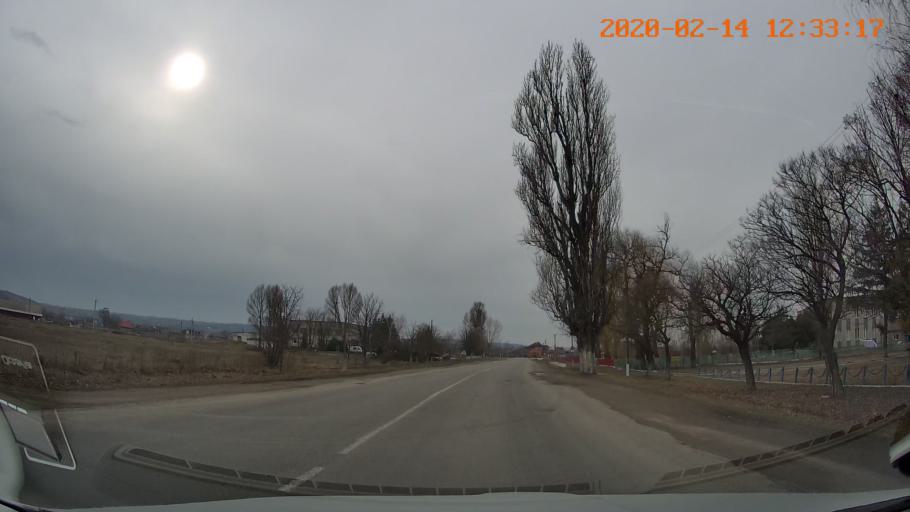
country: RO
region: Botosani
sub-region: Comuna Darabani
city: Bajura
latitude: 48.2344
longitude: 26.5453
